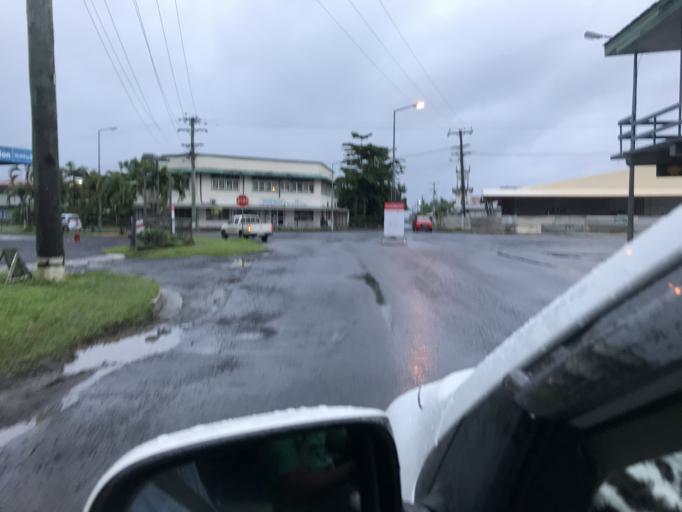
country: WS
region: Tuamasaga
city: Apia
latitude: -13.8335
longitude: -171.7549
